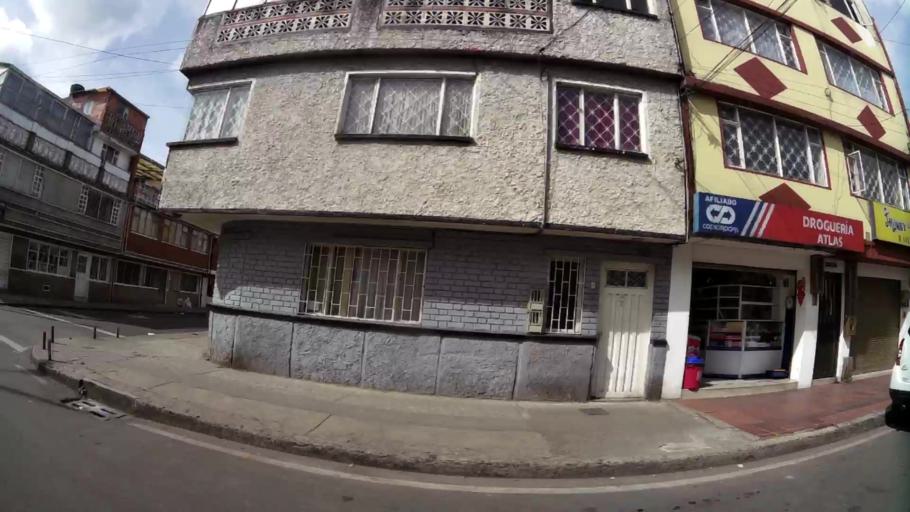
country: CO
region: Bogota D.C.
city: Bogota
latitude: 4.6764
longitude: -74.0940
